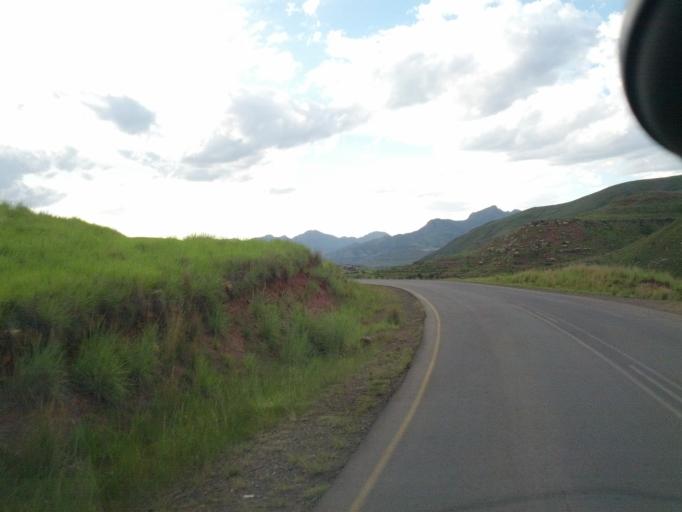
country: LS
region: Qacha's Nek
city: Qacha's Nek
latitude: -30.0989
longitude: 28.6557
